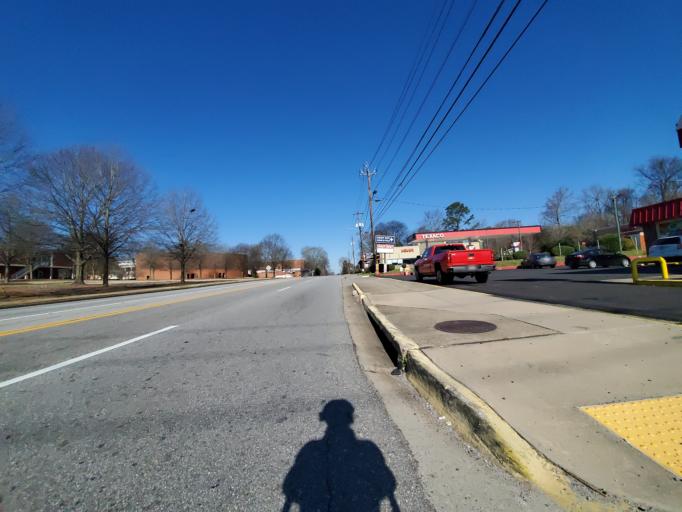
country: US
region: Georgia
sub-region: Clarke County
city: Athens
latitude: 33.9639
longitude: -83.4018
